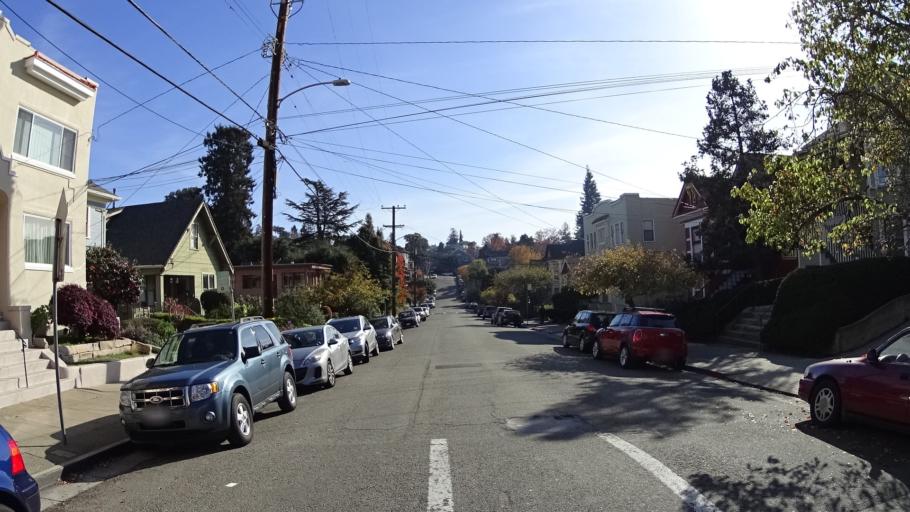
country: US
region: California
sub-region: Alameda County
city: Piedmont
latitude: 37.8236
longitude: -122.2553
